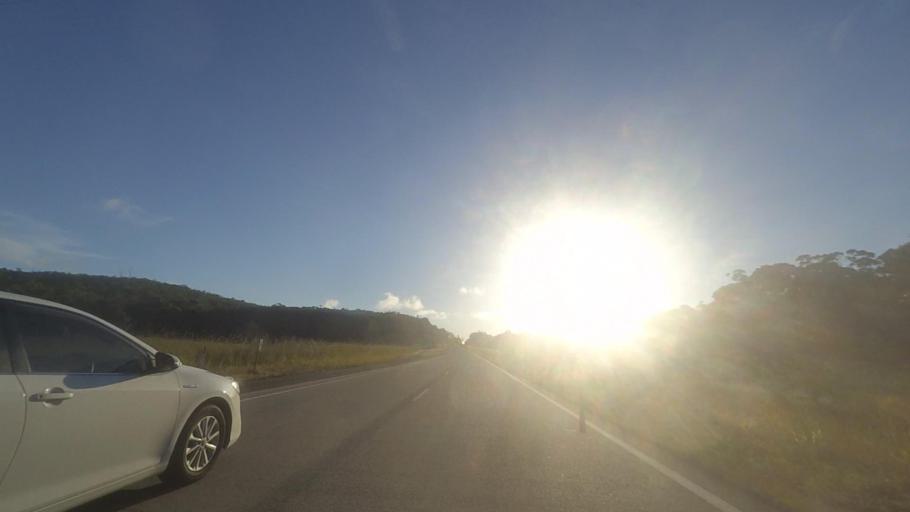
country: AU
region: New South Wales
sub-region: Great Lakes
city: Bulahdelah
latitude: -32.5306
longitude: 152.1855
